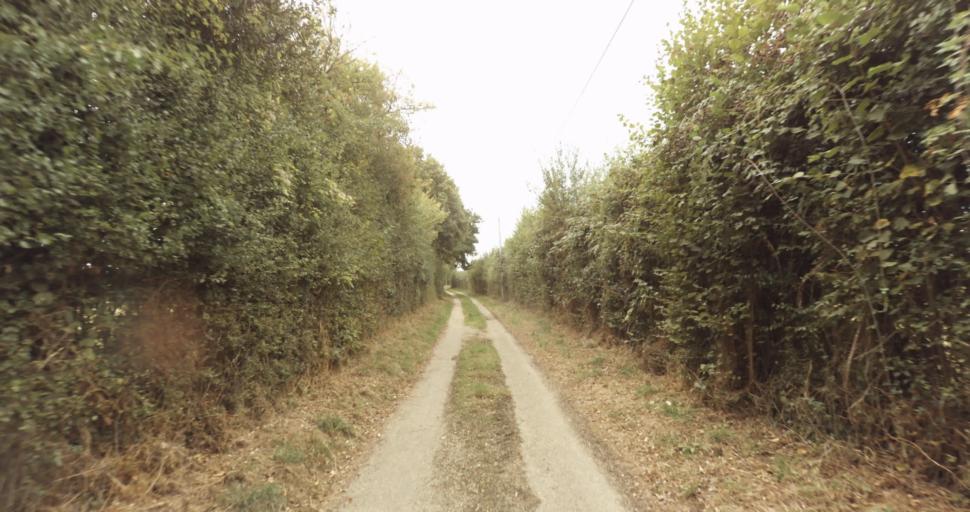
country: FR
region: Lower Normandy
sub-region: Departement du Calvados
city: Orbec
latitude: 48.9123
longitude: 0.3716
